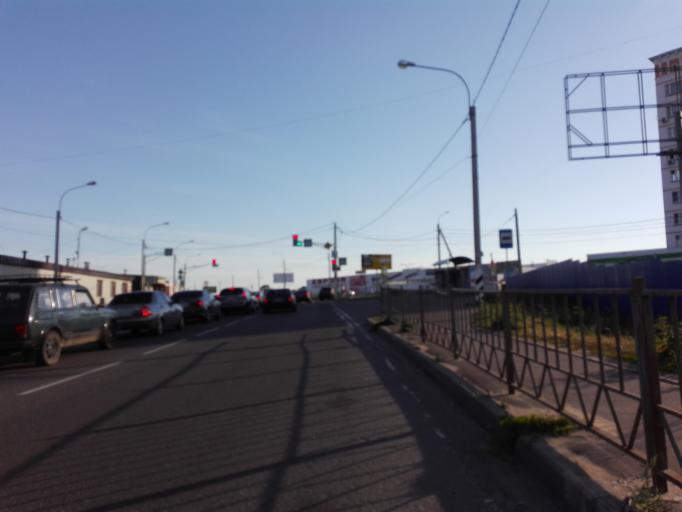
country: RU
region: Orjol
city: Orel
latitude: 52.9499
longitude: 36.0257
